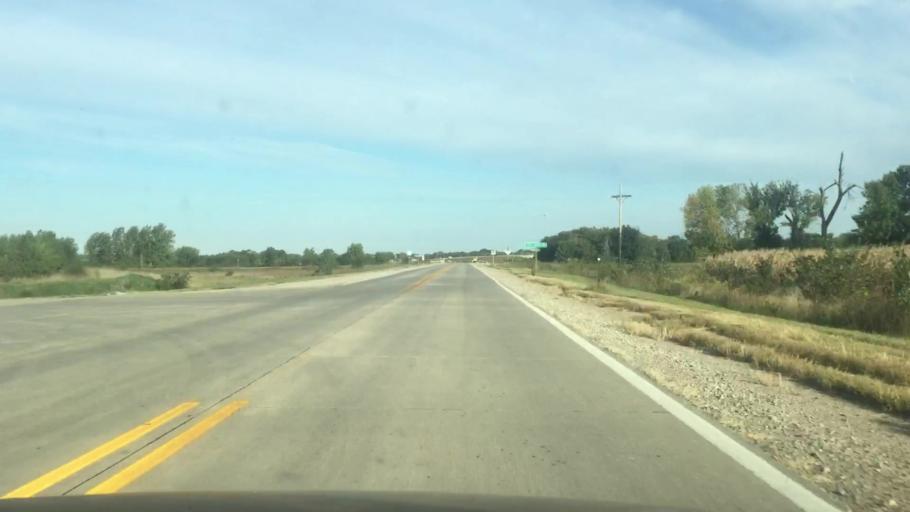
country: US
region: Nebraska
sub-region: Jefferson County
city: Fairbury
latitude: 40.1240
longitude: -97.1609
